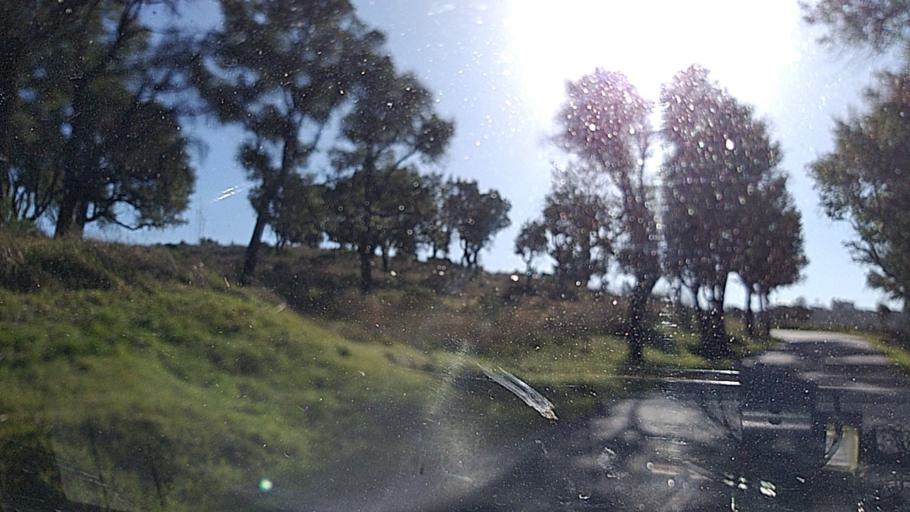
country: PT
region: Guarda
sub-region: Celorico da Beira
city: Celorico da Beira
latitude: 40.6939
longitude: -7.4494
